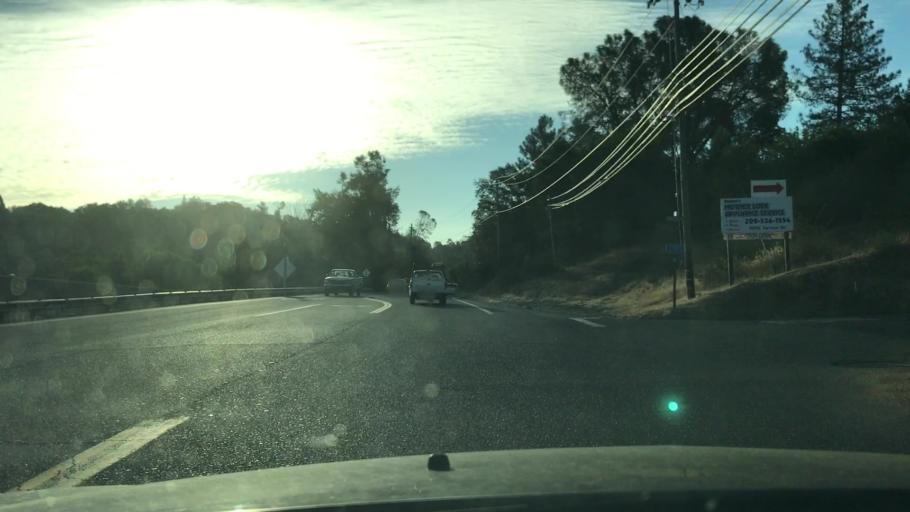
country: US
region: California
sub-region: Tuolumne County
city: East Sonora
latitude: 37.9736
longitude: -120.3430
